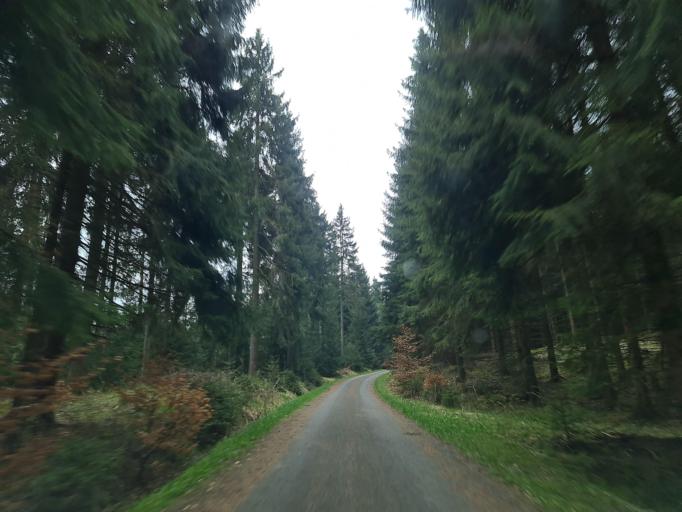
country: DE
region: Saxony
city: Ellefeld
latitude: 50.4594
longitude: 12.3901
